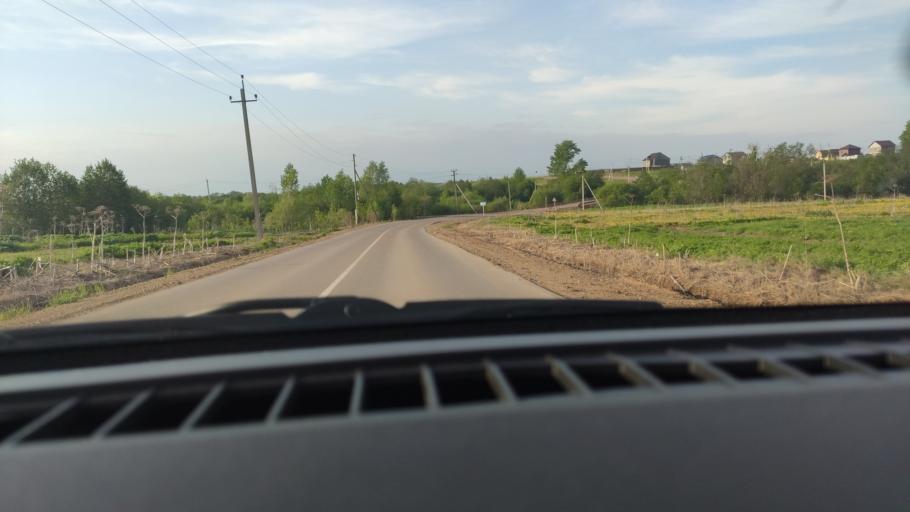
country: RU
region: Perm
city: Kultayevo
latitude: 57.8952
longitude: 55.9915
